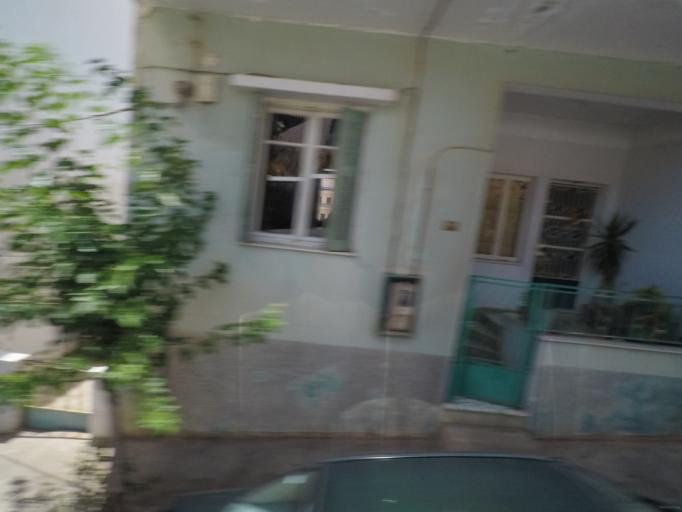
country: GR
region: Crete
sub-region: Nomos Lasithiou
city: Agios Nikolaos
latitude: 35.1933
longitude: 25.7154
